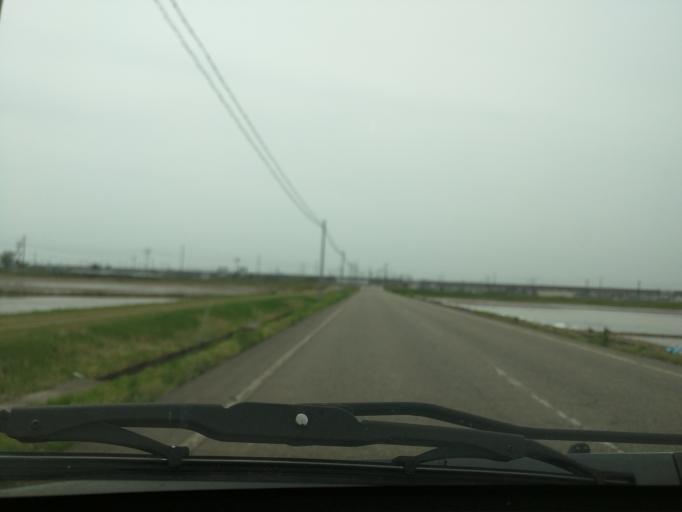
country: JP
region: Niigata
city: Mitsuke
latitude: 37.5506
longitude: 138.9025
